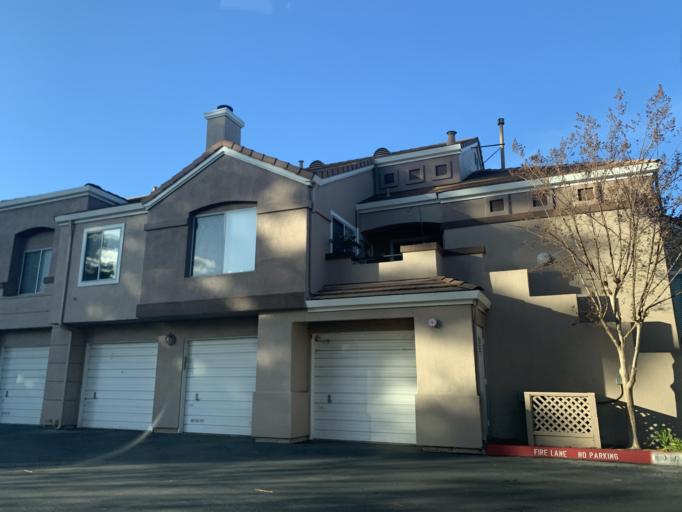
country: US
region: California
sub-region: Santa Clara County
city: Seven Trees
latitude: 37.2372
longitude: -121.7658
